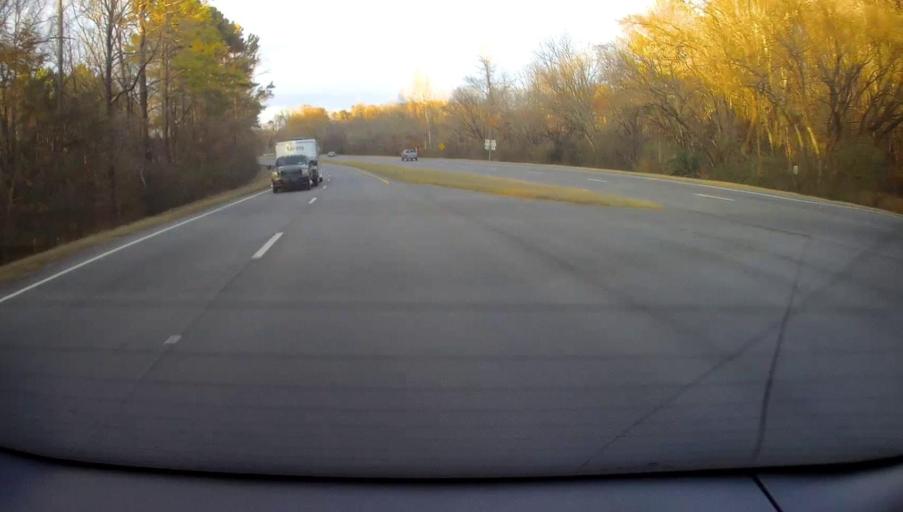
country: US
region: Alabama
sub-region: Etowah County
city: Attalla
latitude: 34.0309
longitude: -86.1105
